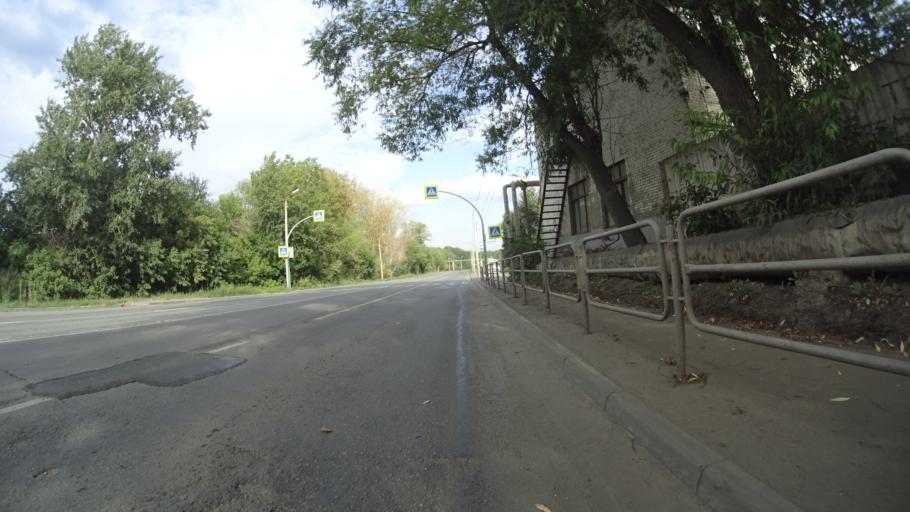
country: RU
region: Chelyabinsk
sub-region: Gorod Chelyabinsk
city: Chelyabinsk
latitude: 55.1959
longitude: 61.3785
